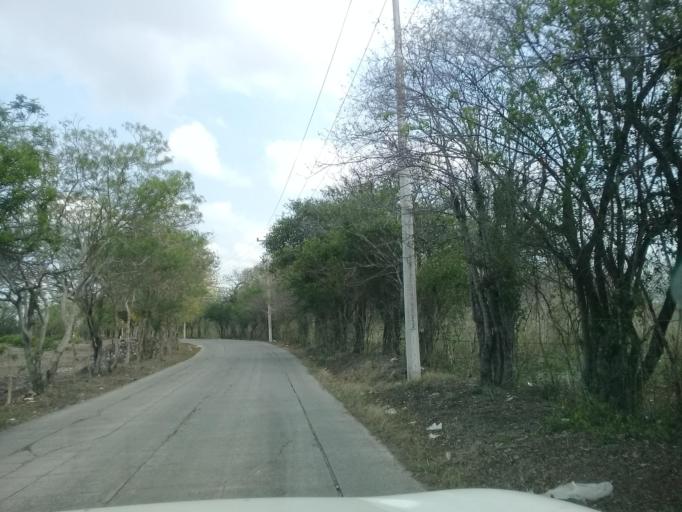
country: MX
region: Veracruz
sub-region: Emiliano Zapata
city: Plan del Rio
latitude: 19.3563
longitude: -96.6523
